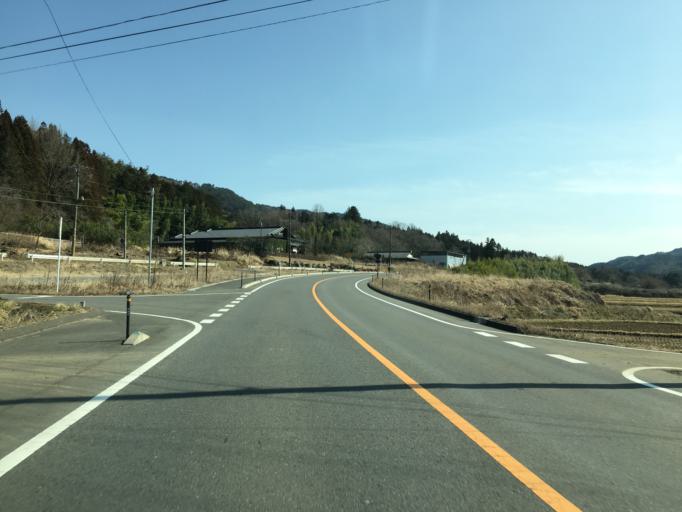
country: JP
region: Ibaraki
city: Daigo
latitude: 36.8309
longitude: 140.4546
